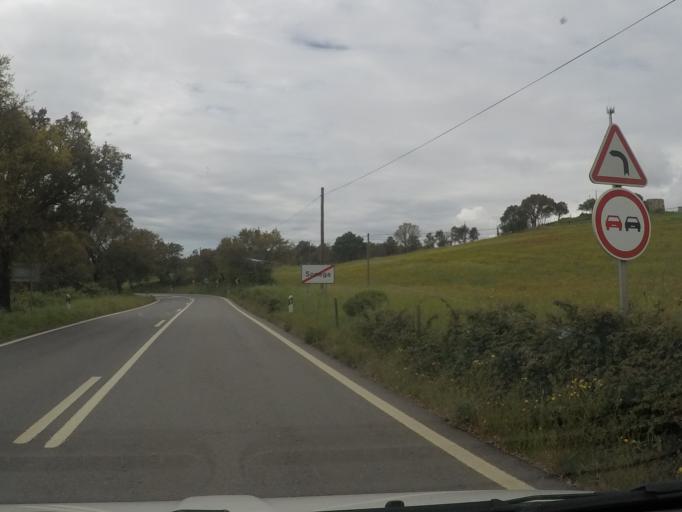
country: PT
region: Setubal
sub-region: Sines
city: Porto Covo
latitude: 37.8674
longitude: -8.7224
